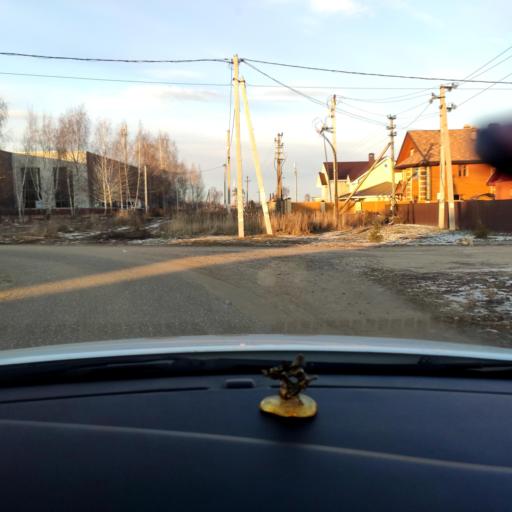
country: RU
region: Tatarstan
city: Stolbishchi
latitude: 55.6098
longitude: 49.1488
